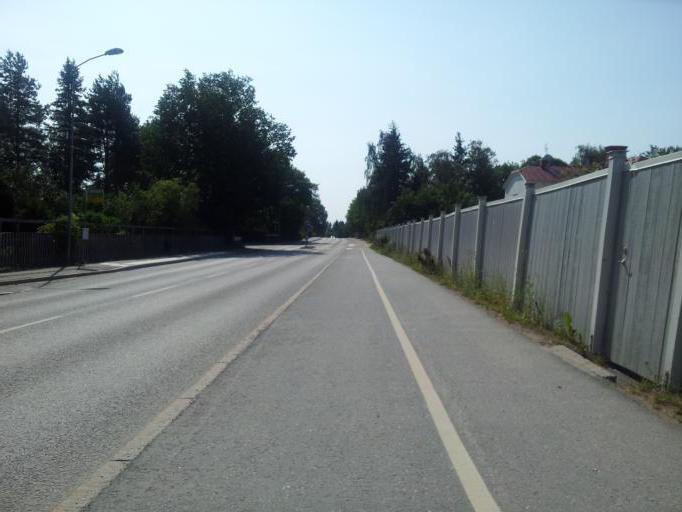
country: SE
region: Uppsala
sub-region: Uppsala Kommun
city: Gamla Uppsala
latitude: 59.8954
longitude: 17.6365
